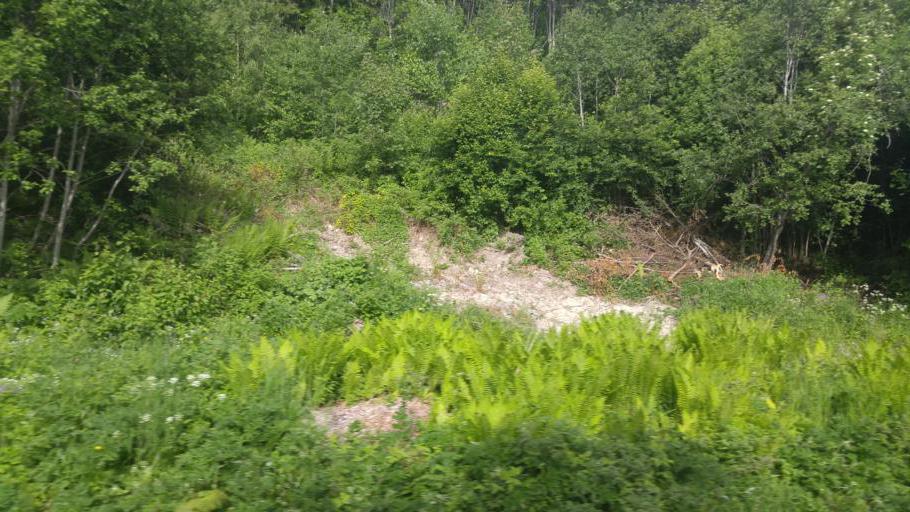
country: NO
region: Sor-Trondelag
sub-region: Trondheim
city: Trondheim
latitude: 63.3934
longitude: 10.3807
